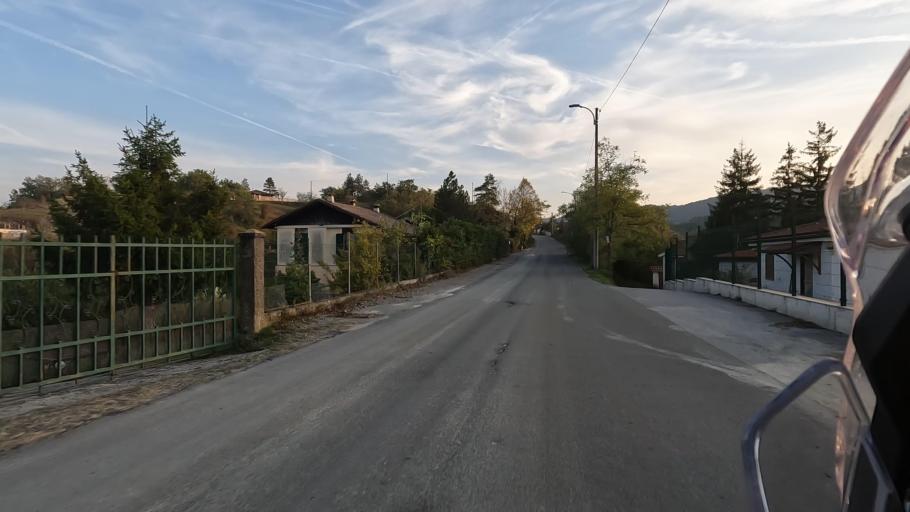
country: IT
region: Liguria
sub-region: Provincia di Savona
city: Mioglia
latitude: 44.4829
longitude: 8.4132
